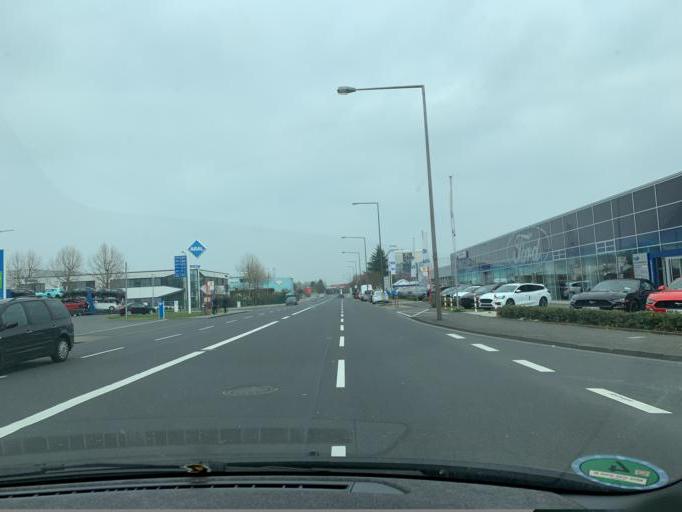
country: DE
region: North Rhine-Westphalia
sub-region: Regierungsbezirk Koln
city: Bilderstoeckchen
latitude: 51.0321
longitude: 6.9195
